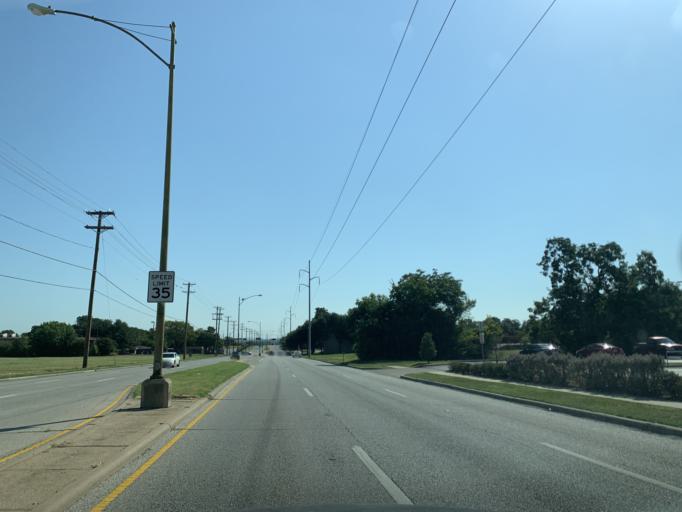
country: US
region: Texas
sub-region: Dallas County
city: Hutchins
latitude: 32.6732
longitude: -96.7618
